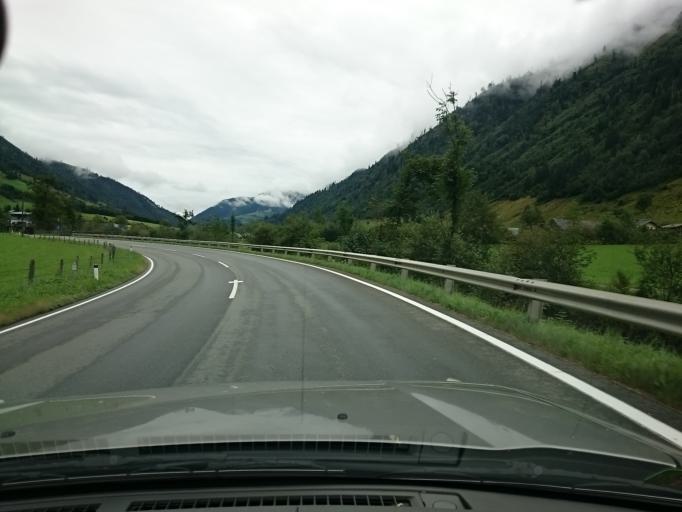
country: AT
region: Salzburg
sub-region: Politischer Bezirk Zell am See
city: Bruck an der Grossglocknerstrasse
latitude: 47.2353
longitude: 12.8263
